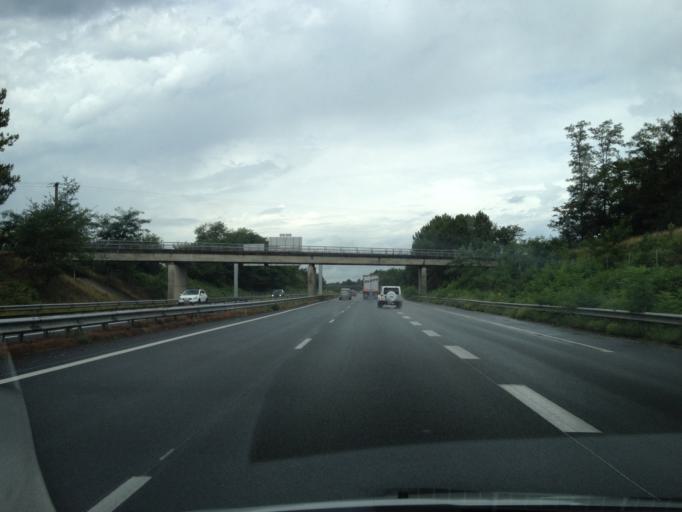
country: FR
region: Aquitaine
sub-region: Departement de la Gironde
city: Toulenne
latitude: 44.5444
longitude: -0.2673
